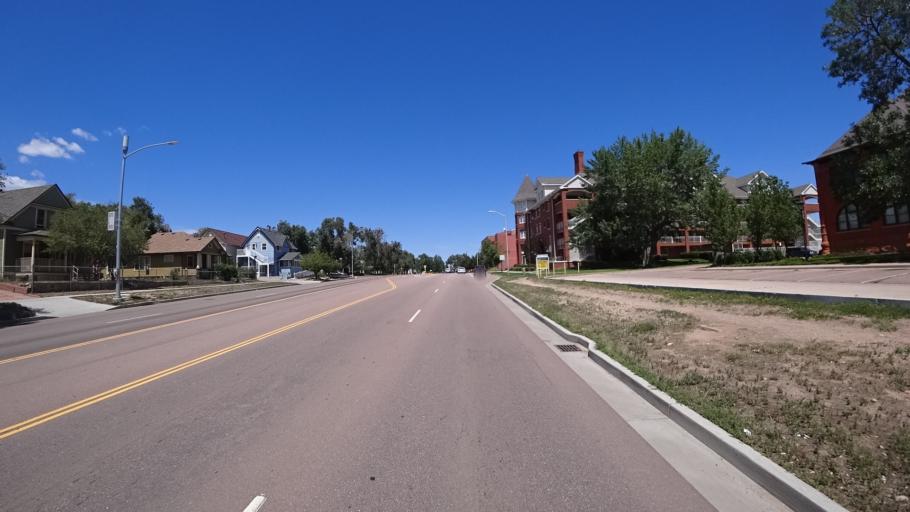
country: US
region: Colorado
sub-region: El Paso County
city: Colorado Springs
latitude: 38.8222
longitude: -104.8222
